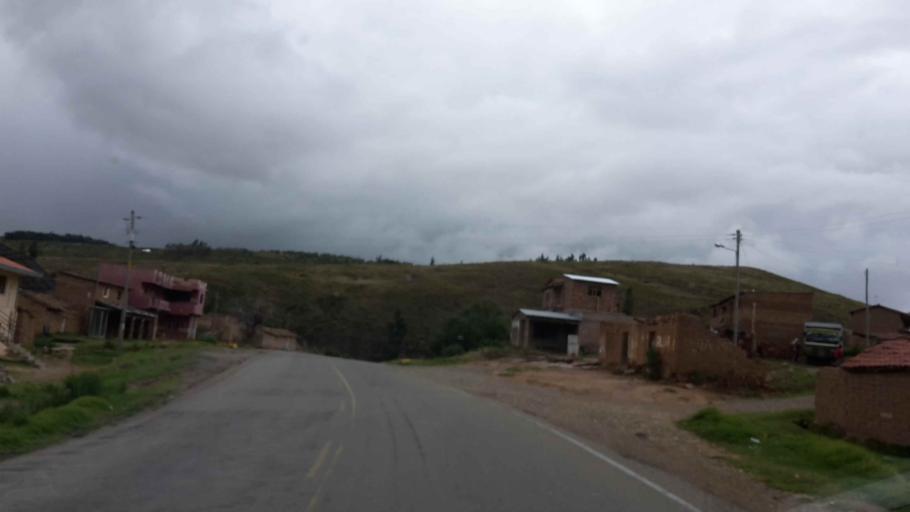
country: BO
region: Cochabamba
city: Arani
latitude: -17.4800
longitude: -65.7650
